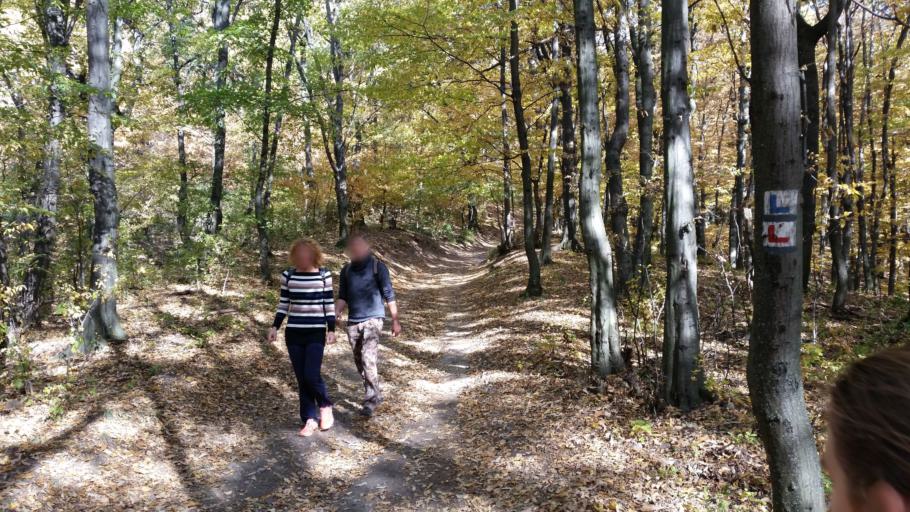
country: HU
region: Nograd
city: Nagyoroszi
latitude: 48.0150
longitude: 19.0361
